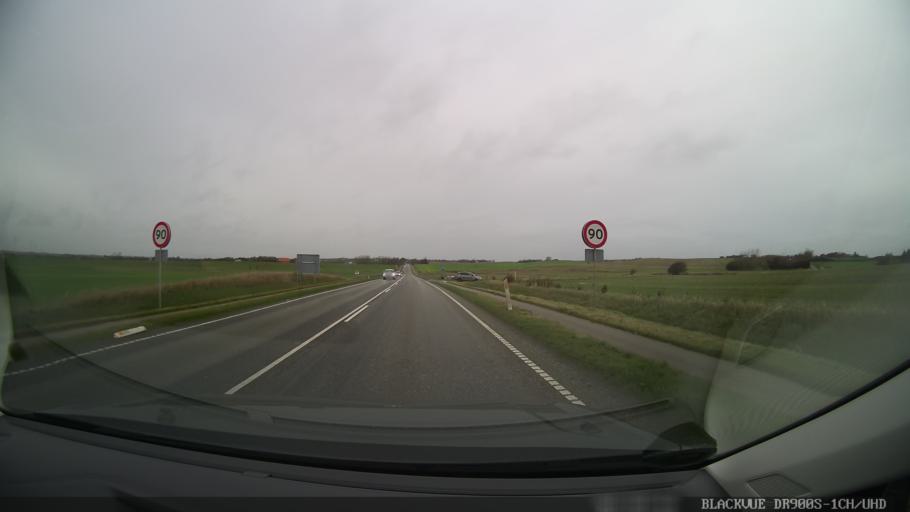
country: DK
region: North Denmark
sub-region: Thisted Kommune
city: Thisted
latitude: 56.8570
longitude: 8.6950
